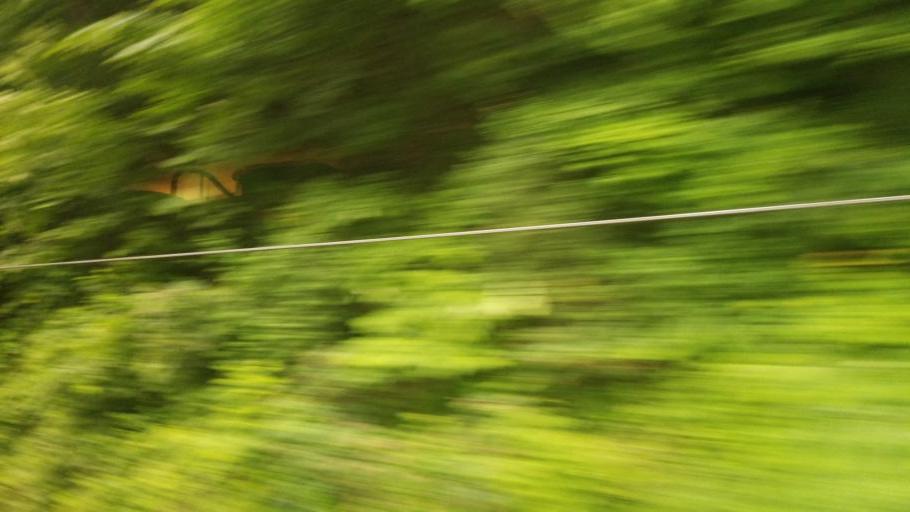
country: US
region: Pennsylvania
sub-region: Somerset County
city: Milford
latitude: 39.8186
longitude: -79.3217
